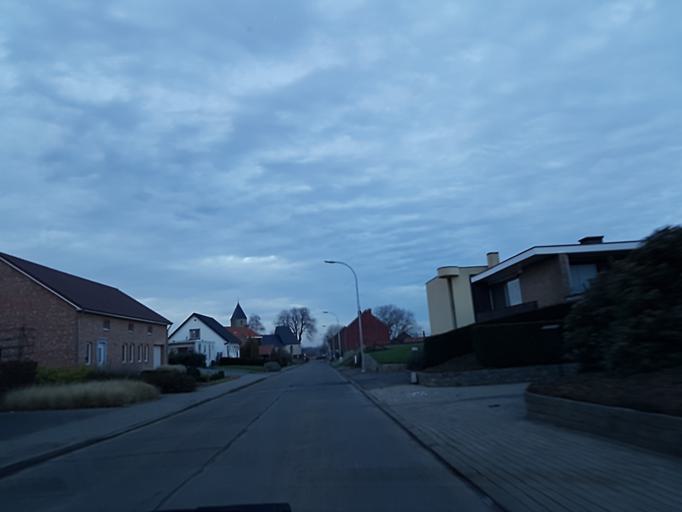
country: BE
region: Flanders
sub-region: Provincie Vlaams-Brabant
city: Boutersem
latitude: 50.8321
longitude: 4.8835
